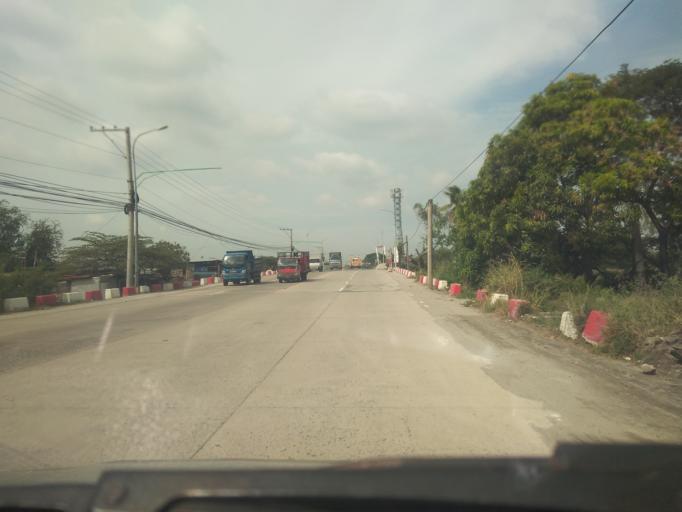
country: PH
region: Central Luzon
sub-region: Province of Pampanga
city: Pau
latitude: 15.0042
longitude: 120.7200
